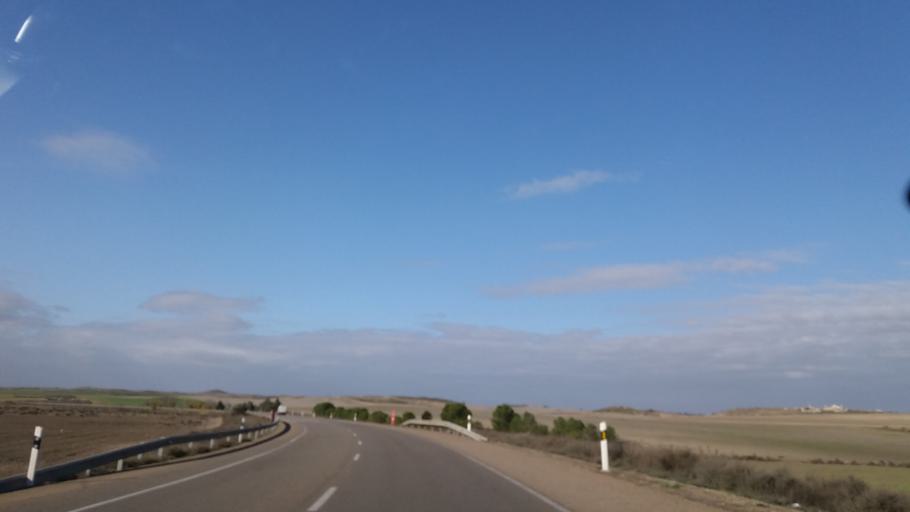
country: ES
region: Aragon
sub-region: Provincia de Huesca
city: Castejon de Monegros
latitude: 41.4994
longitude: -0.2780
